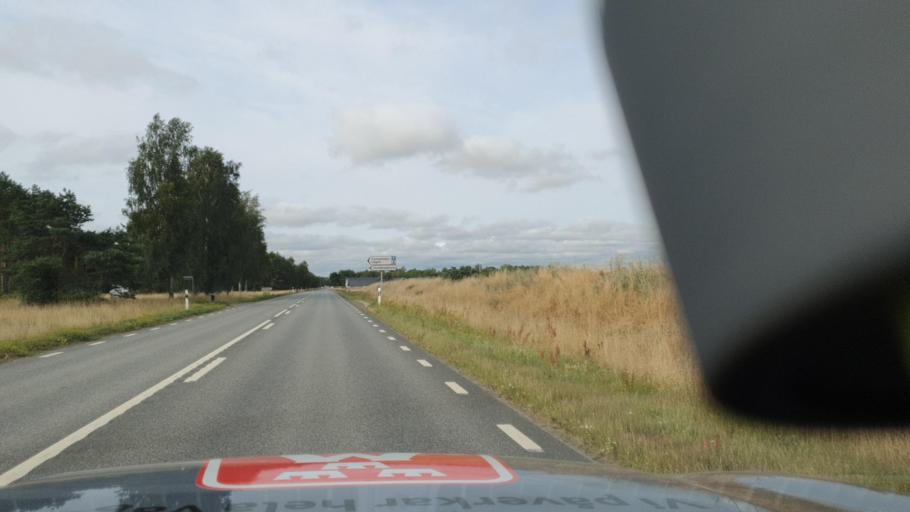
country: SE
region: Skane
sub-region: Kristianstads Kommun
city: Ahus
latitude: 55.8994
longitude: 14.2574
